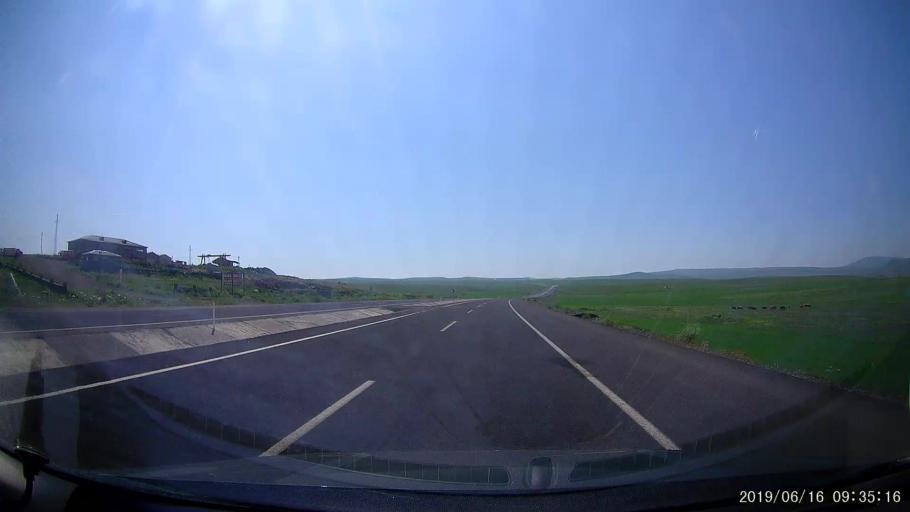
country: TR
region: Kars
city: Kars
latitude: 40.5744
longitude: 43.1530
